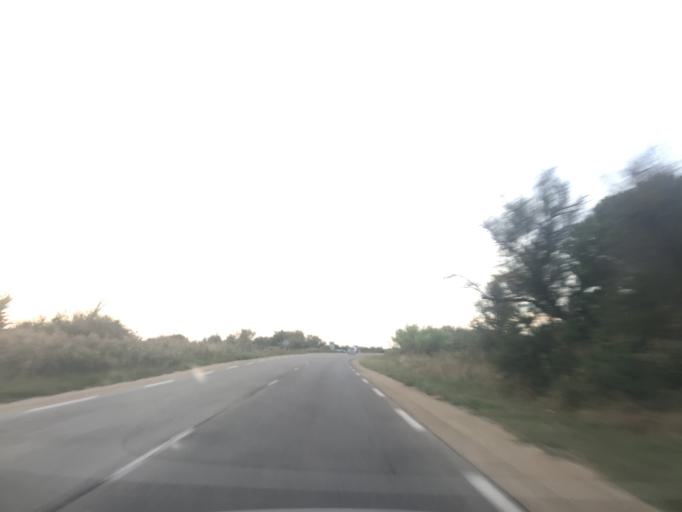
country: FR
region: Provence-Alpes-Cote d'Azur
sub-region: Departement des Bouches-du-Rhone
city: Saintes-Maries-de-la-Mer
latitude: 43.5023
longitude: 4.4018
